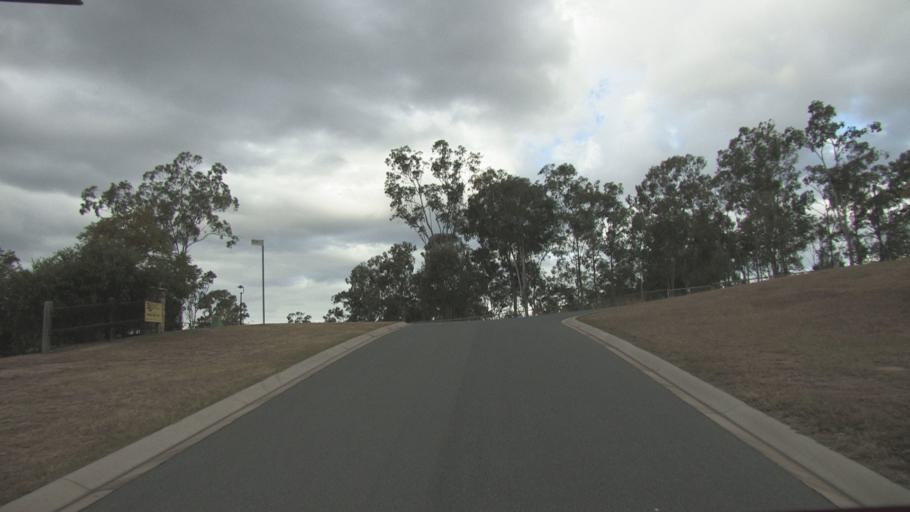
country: AU
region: Queensland
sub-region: Logan
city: Cedar Vale
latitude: -27.8658
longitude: 153.0752
